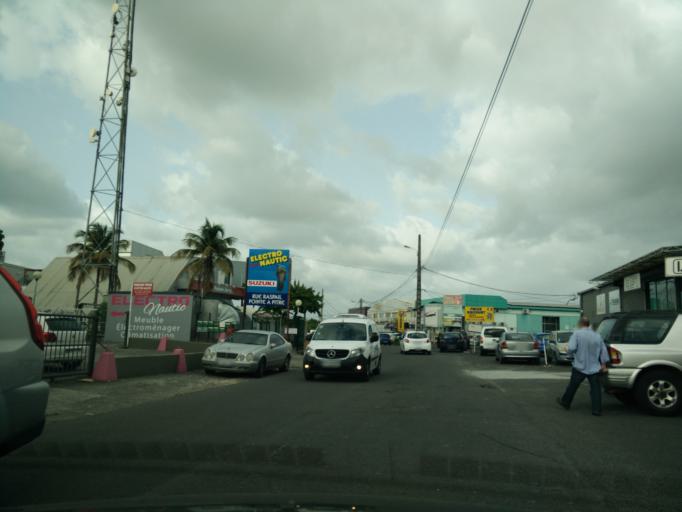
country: GP
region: Guadeloupe
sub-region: Guadeloupe
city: Pointe-a-Pitre
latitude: 16.2395
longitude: -61.5668
